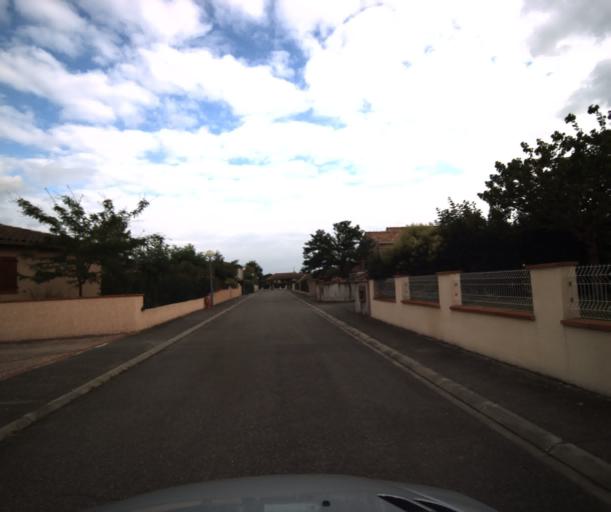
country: FR
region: Midi-Pyrenees
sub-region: Departement de la Haute-Garonne
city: Labarthe-sur-Leze
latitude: 43.4499
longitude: 1.3988
